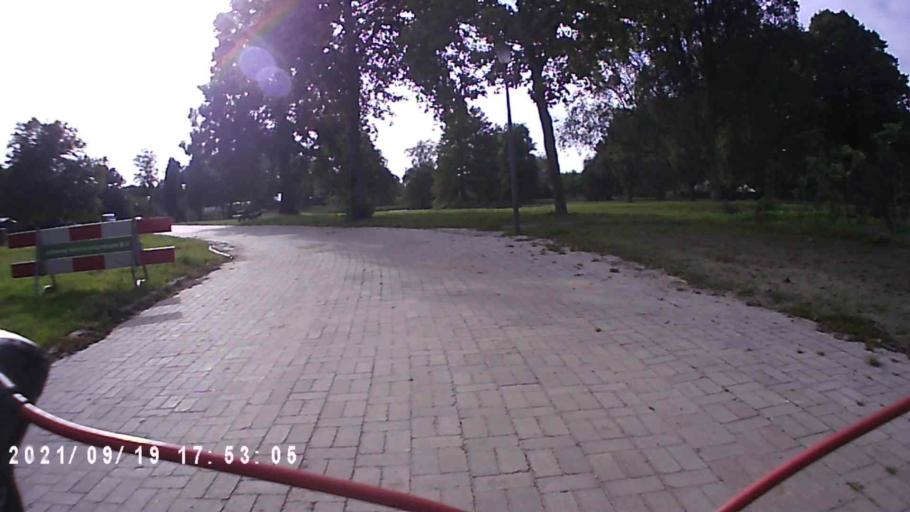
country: NL
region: Groningen
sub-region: Gemeente Delfzijl
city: Delfzijl
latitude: 53.2575
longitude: 6.9410
